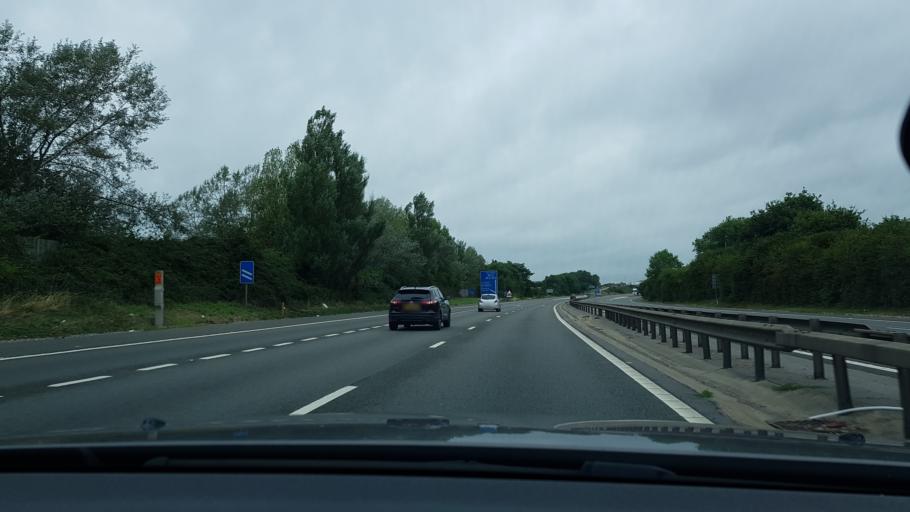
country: GB
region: England
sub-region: Hampshire
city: Totton
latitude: 50.9266
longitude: -1.4723
